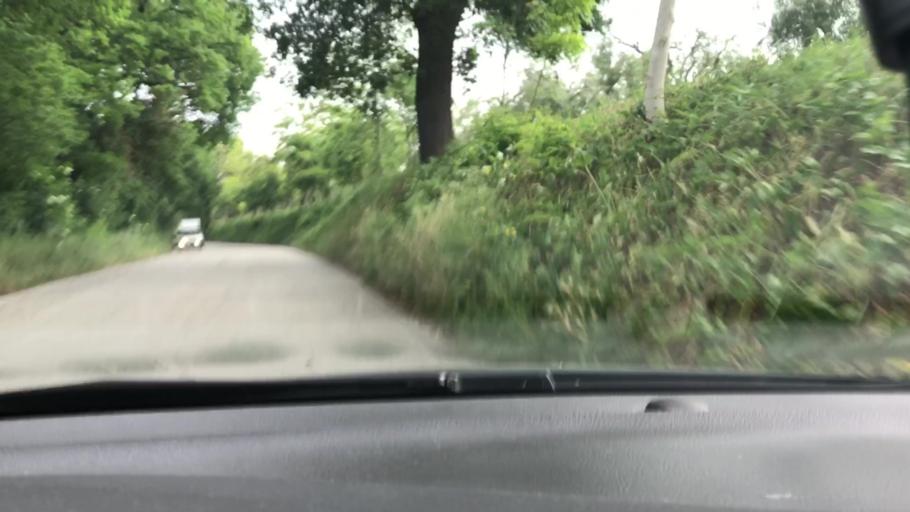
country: IT
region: The Marches
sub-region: Provincia di Macerata
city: Macerata
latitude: 43.2753
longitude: 13.4500
